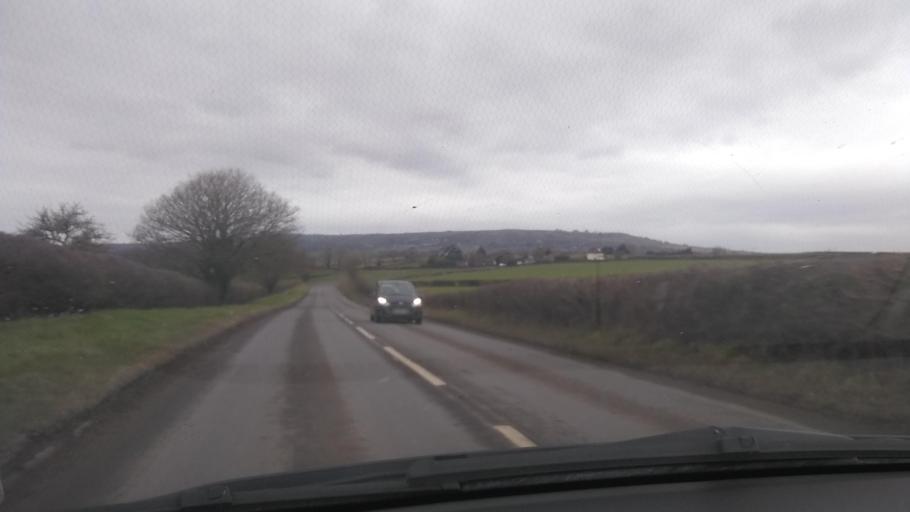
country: GB
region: England
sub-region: Shropshire
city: Cleobury Mortimer
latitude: 52.3762
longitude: -2.5080
